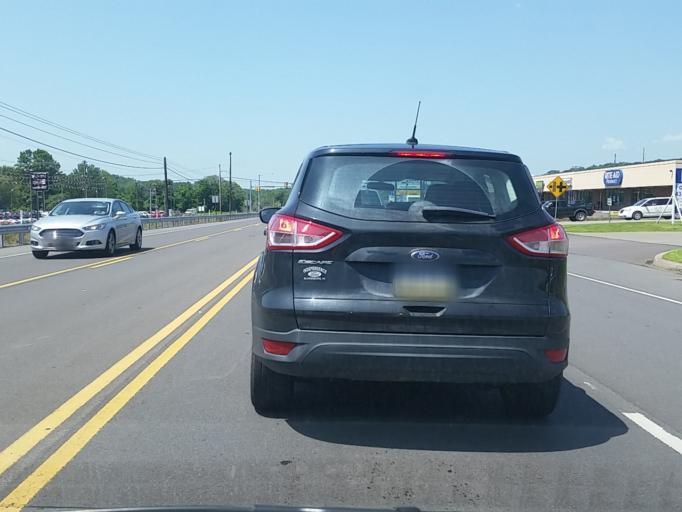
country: US
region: Pennsylvania
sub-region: Columbia County
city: Espy
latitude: 41.0116
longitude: -76.4124
